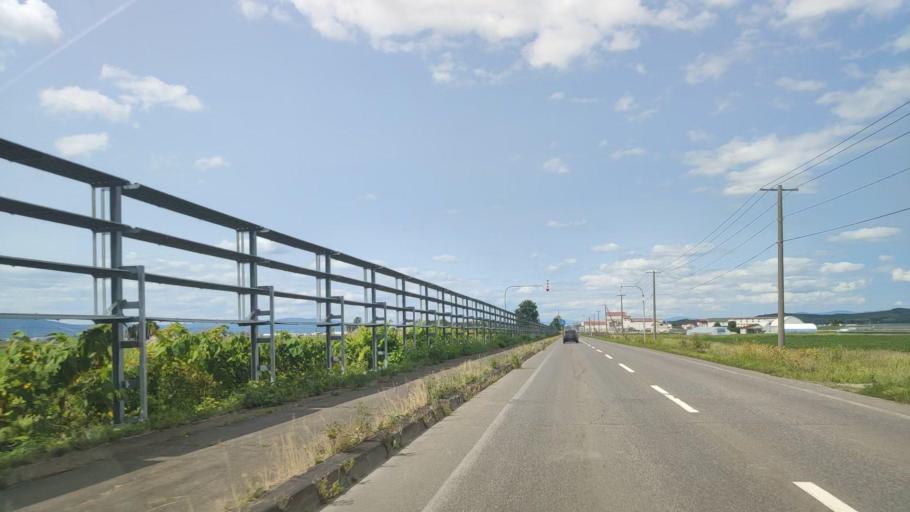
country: JP
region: Hokkaido
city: Nayoro
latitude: 44.1970
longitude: 142.4159
